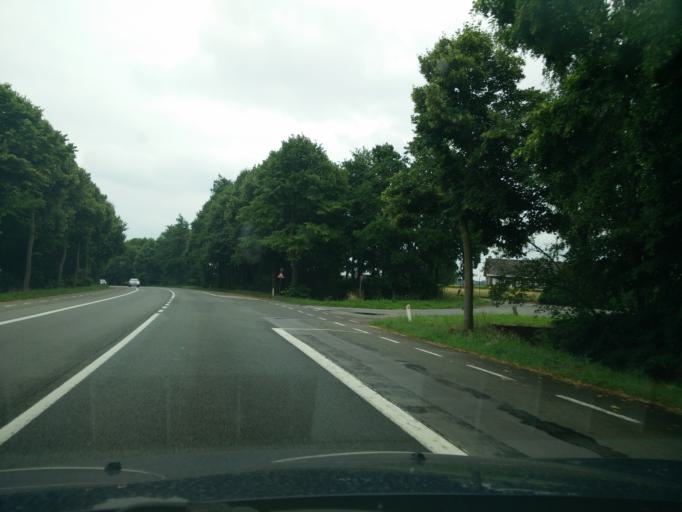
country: BE
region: Wallonia
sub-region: Province du Hainaut
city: Ellezelles
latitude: 50.8196
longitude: 3.7037
